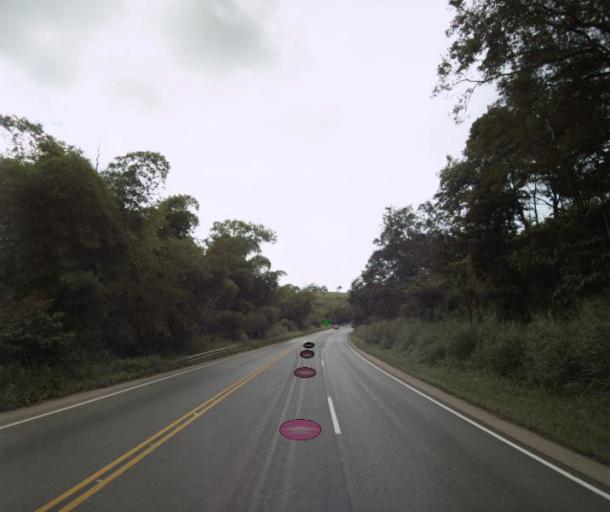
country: BR
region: Goias
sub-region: Rialma
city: Rialma
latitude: -15.2488
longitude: -49.5567
